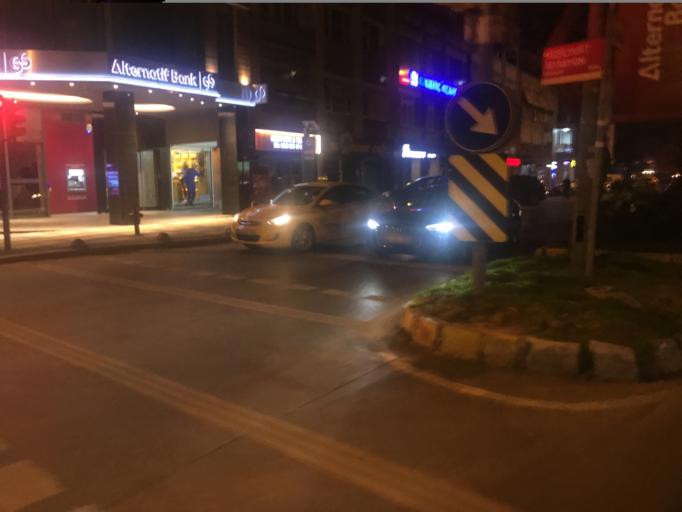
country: TR
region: Istanbul
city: Bahcelievler
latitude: 40.9648
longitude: 28.8371
